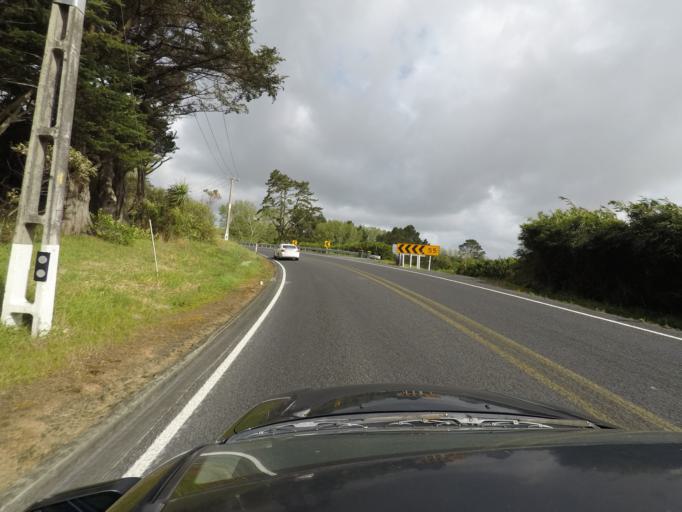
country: NZ
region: Auckland
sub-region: Auckland
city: Pakuranga
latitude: -36.9293
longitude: 174.9361
